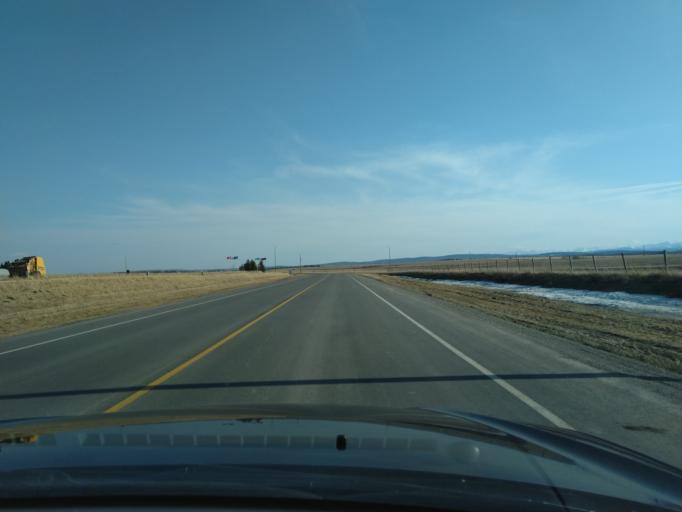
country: CA
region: Alberta
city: Cochrane
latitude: 51.0984
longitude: -114.3886
